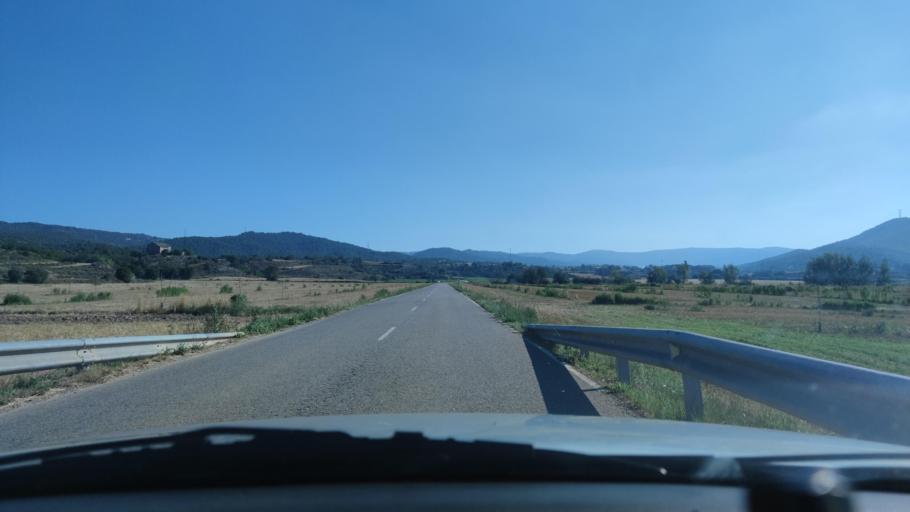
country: ES
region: Catalonia
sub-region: Provincia de Lleida
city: Ponts
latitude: 41.9045
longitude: 1.2421
